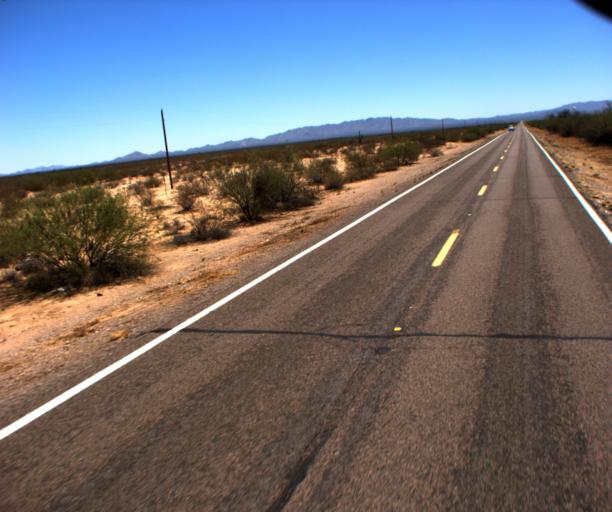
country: US
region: Arizona
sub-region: Pima County
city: Ajo
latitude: 32.1955
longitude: -112.4558
